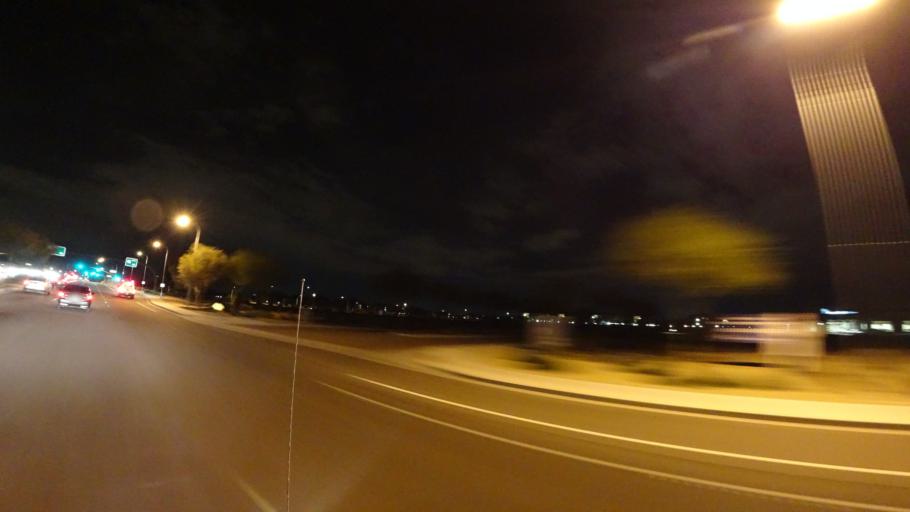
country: US
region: Arizona
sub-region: Maricopa County
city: Chandler
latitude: 33.2849
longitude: -111.8588
